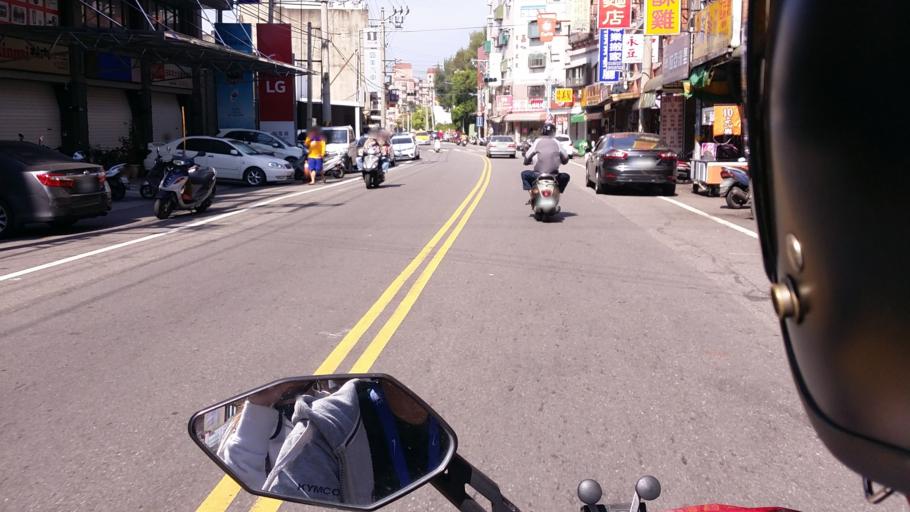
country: TW
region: Taiwan
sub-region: Hsinchu
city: Hsinchu
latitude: 24.7884
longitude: 120.9670
